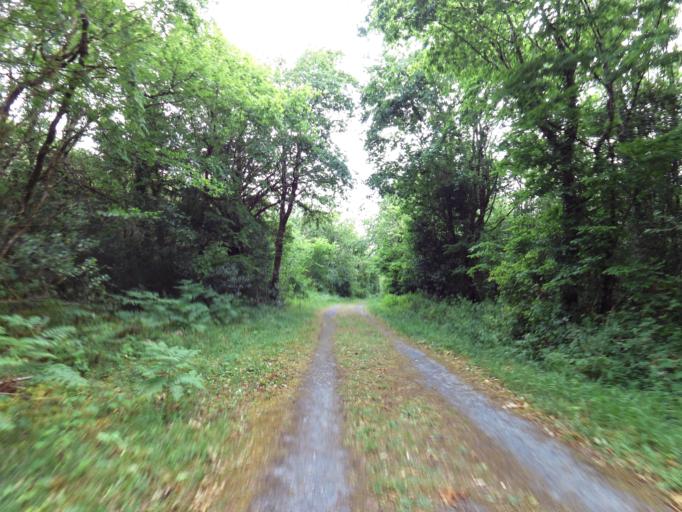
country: IE
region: Connaught
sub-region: County Galway
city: Gort
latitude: 53.0825
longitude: -8.8674
